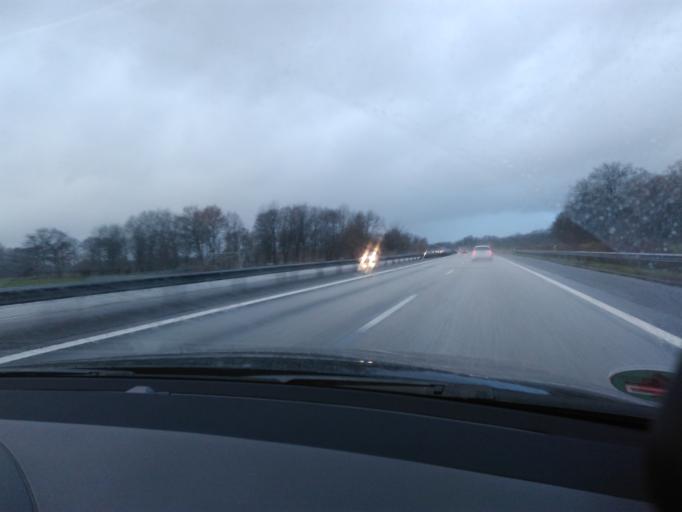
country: DE
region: Schleswig-Holstein
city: Schmalfeld
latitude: 53.8700
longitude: 9.9472
